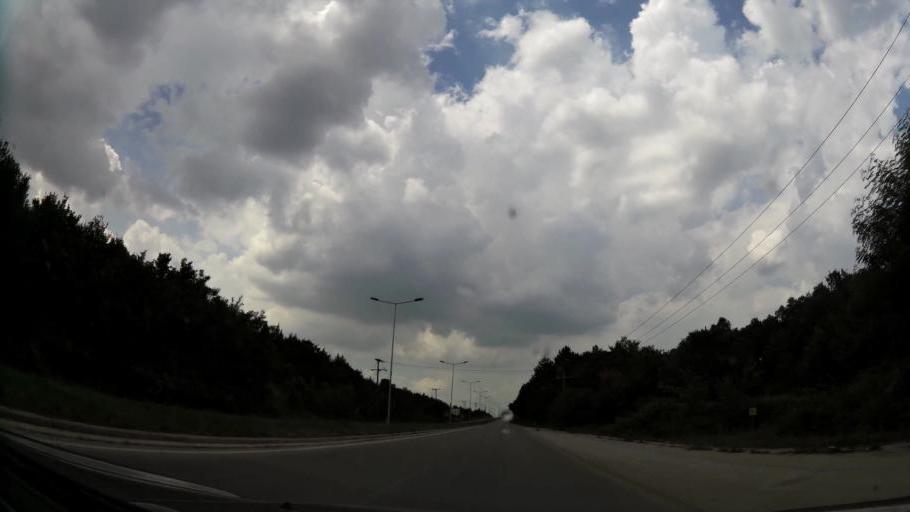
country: GR
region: West Macedonia
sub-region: Nomos Kozanis
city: Koila
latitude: 40.3229
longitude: 21.8277
